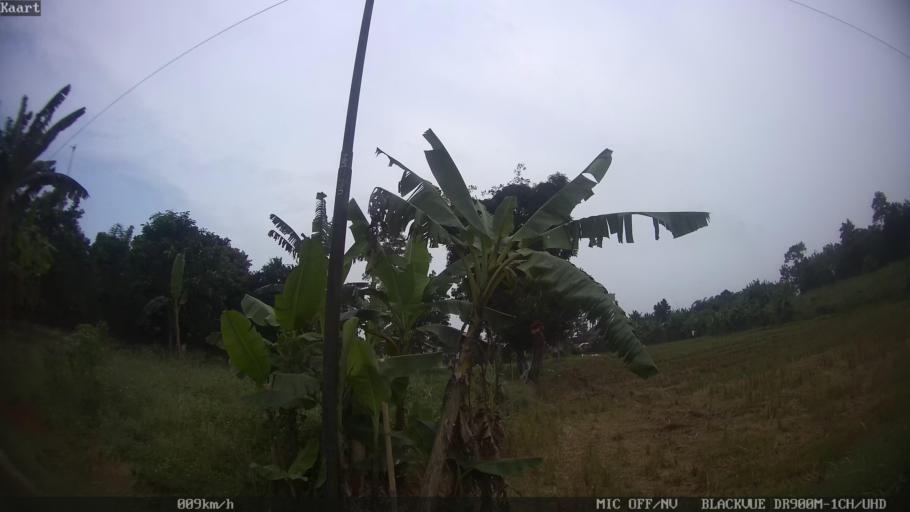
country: ID
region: Lampung
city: Panjang
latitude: -5.4132
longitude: 105.3567
